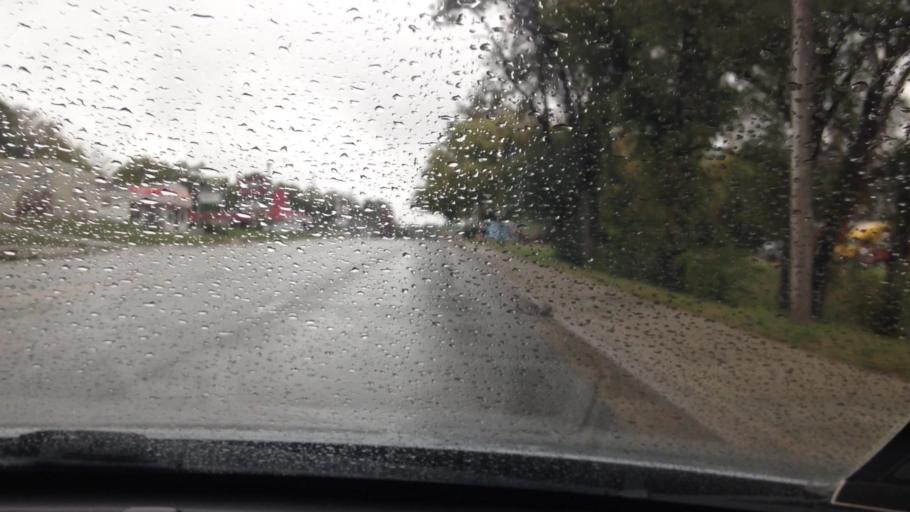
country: US
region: Kansas
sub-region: Leavenworth County
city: Leavenworth
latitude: 39.2974
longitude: -94.9089
